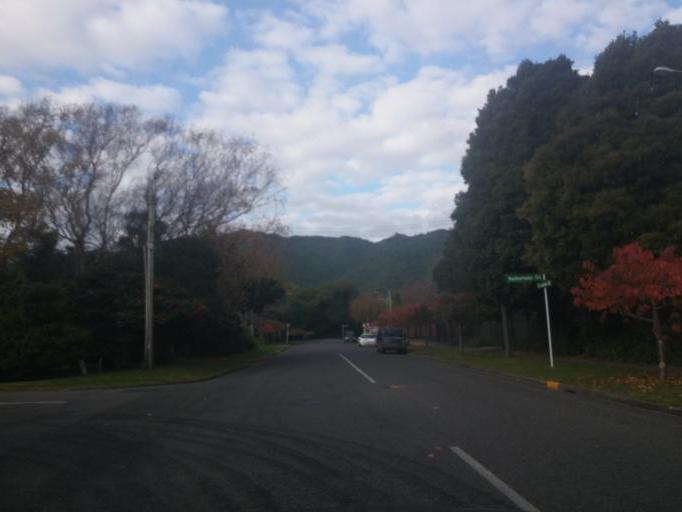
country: NZ
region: Wellington
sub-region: Kapiti Coast District
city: Paraparaumu
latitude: -40.8766
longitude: 175.0595
